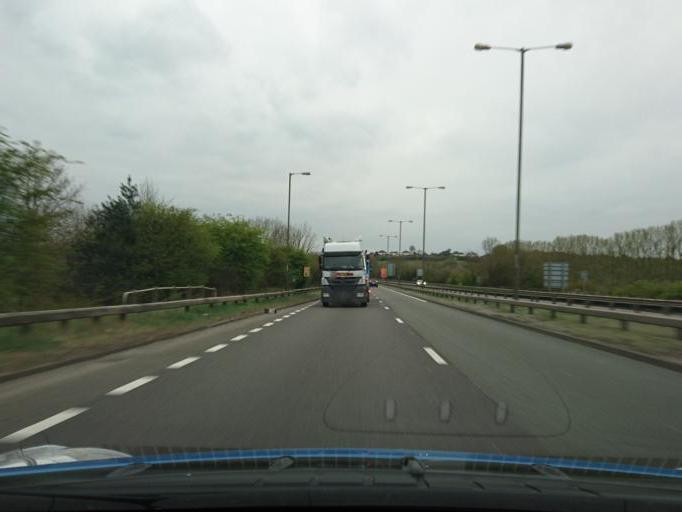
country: GB
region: England
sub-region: Stoke-on-Trent
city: Stoke-on-Trent
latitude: 52.9810
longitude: -2.2046
